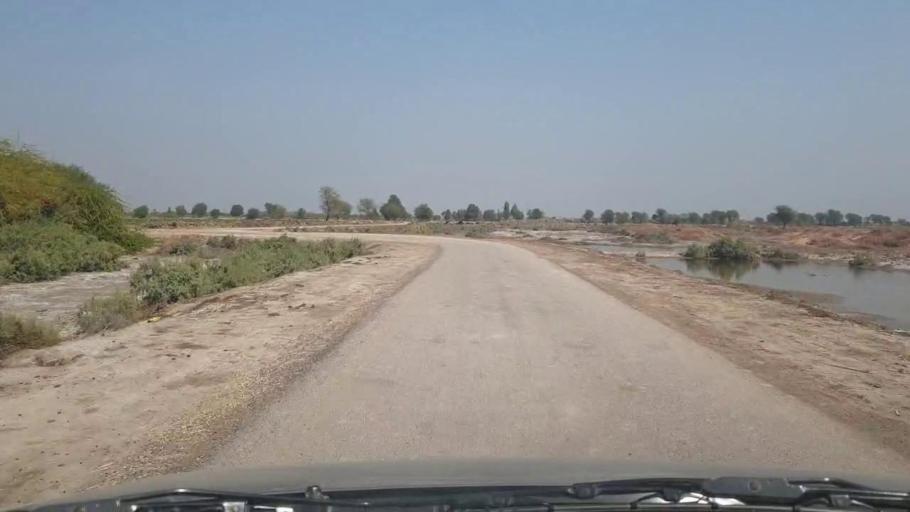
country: PK
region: Sindh
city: Mirwah Gorchani
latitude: 25.3379
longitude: 69.1487
